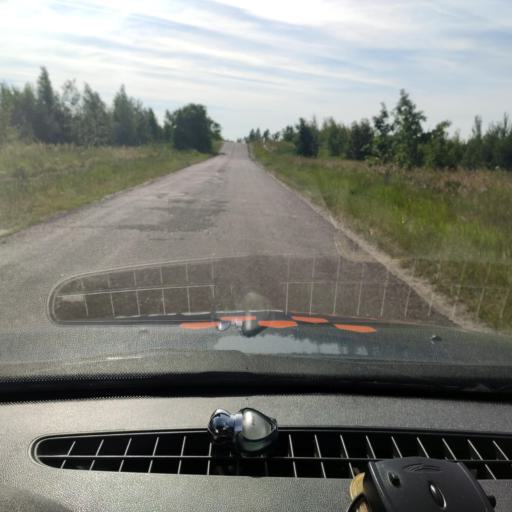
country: RU
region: Voronezj
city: Somovo
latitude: 51.7824
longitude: 39.3831
